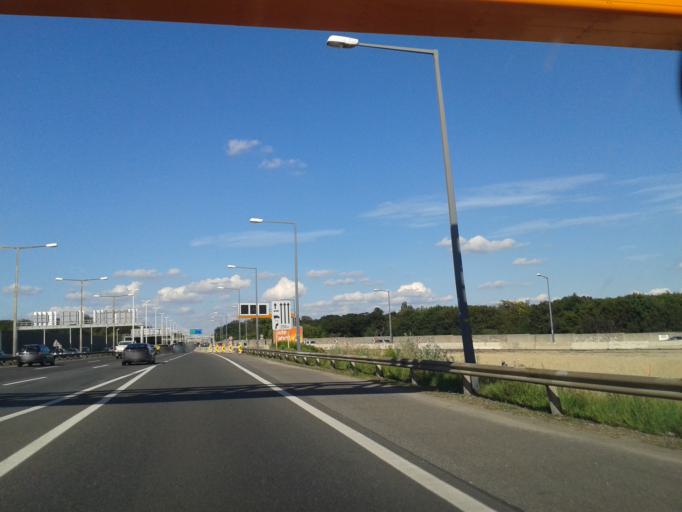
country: AT
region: Vienna
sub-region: Wien Stadt
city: Vienna
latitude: 48.1940
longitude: 16.4181
